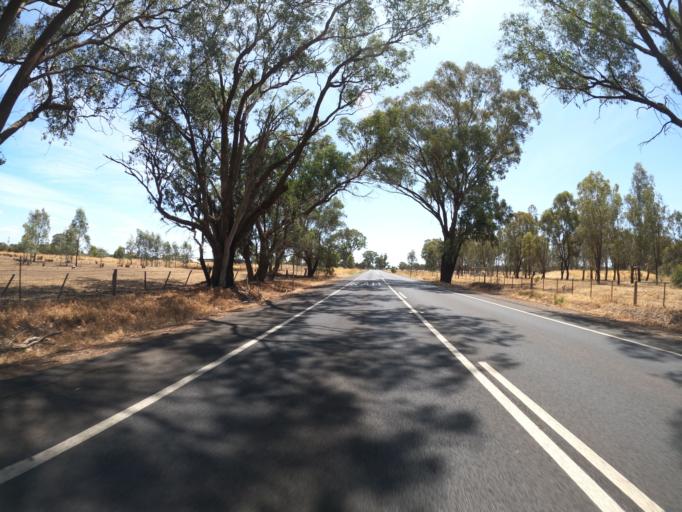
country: AU
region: Victoria
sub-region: Benalla
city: Benalla
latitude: -36.5248
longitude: 146.0376
